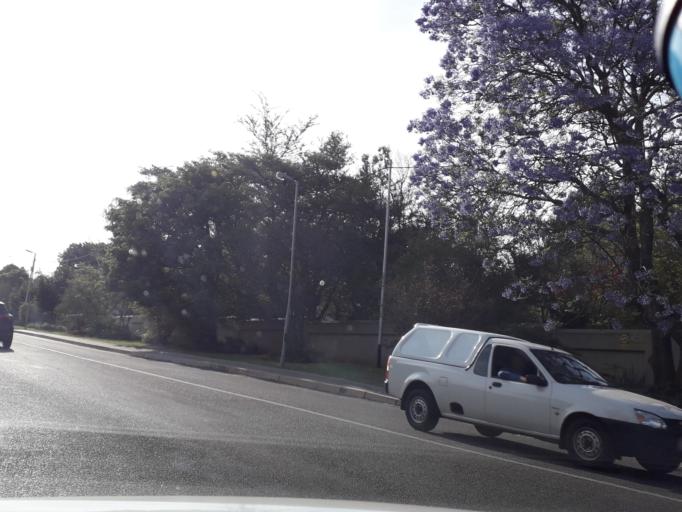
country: ZA
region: Gauteng
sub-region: City of Johannesburg Metropolitan Municipality
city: Johannesburg
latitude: -26.0712
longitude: 28.0200
